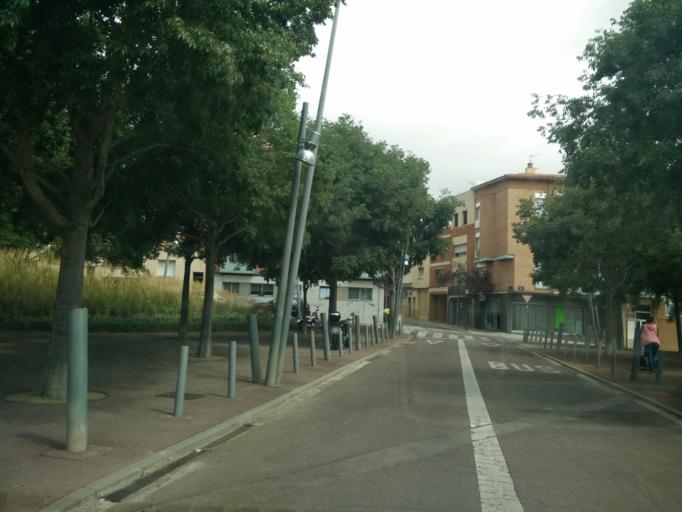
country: ES
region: Catalonia
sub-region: Provincia de Barcelona
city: Terrassa
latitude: 41.5707
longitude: 2.0146
